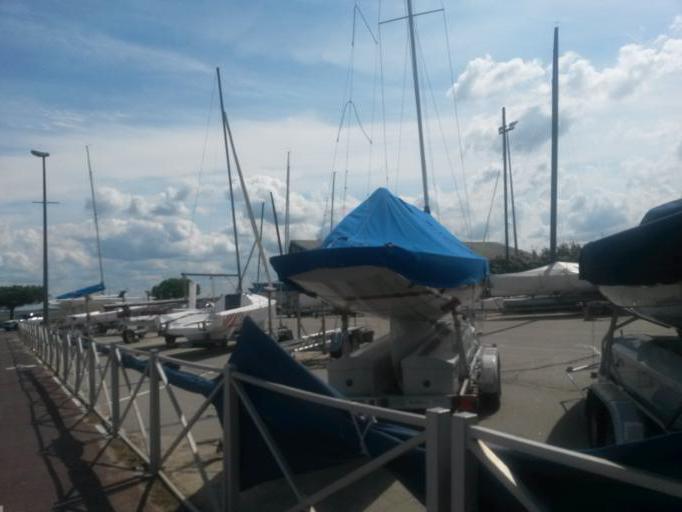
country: FR
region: Aquitaine
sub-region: Departement de la Gironde
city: Arcachon
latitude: 44.6596
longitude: -1.1430
